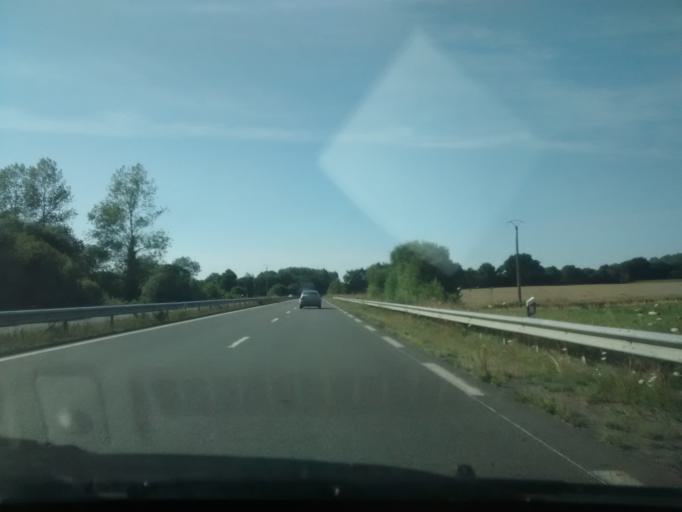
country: FR
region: Brittany
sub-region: Departement des Cotes-d'Armor
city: Cavan
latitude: 48.6642
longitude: -3.3441
